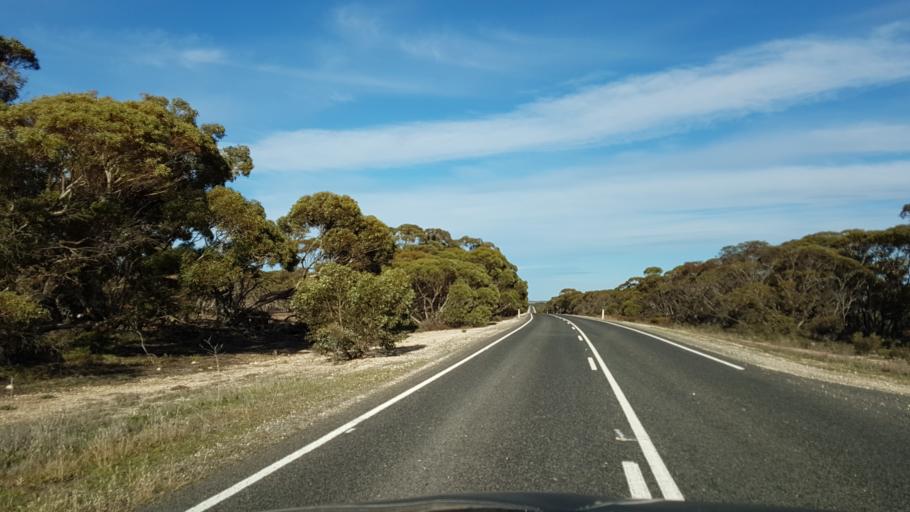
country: AU
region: South Australia
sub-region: Mid Murray
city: Mannum
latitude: -34.9856
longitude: 139.5736
